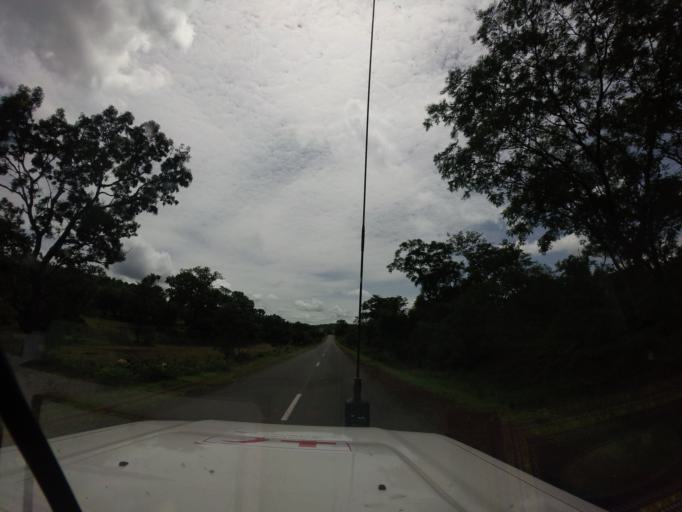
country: SL
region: Northern Province
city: Gberia Fotombu
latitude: 10.0467
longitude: -10.9963
